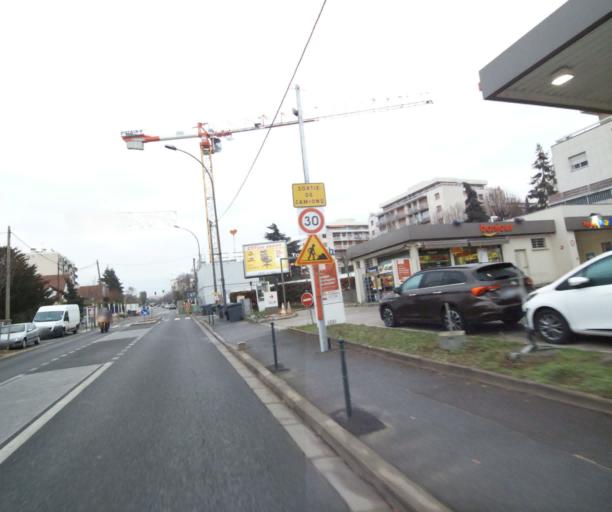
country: FR
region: Ile-de-France
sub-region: Departement des Hauts-de-Seine
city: Rueil-Malmaison
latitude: 48.8683
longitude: 2.1907
